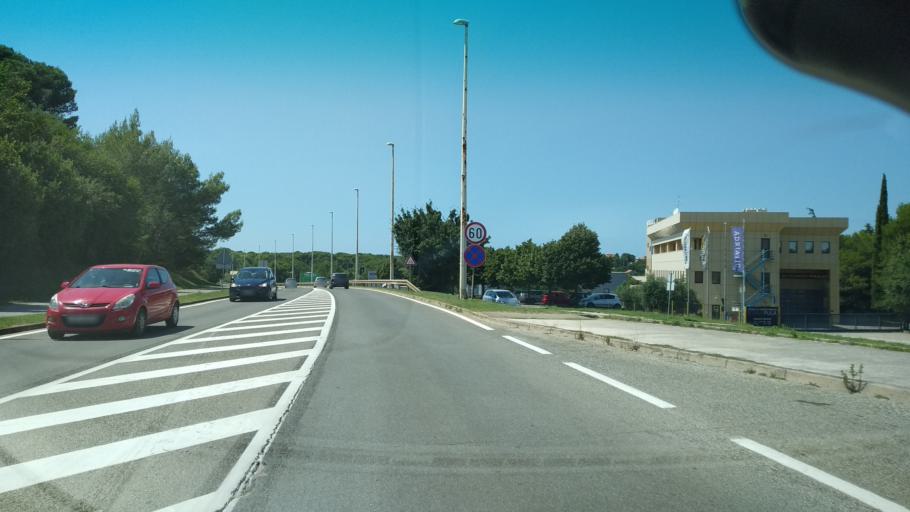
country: HR
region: Istarska
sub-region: Grad Pula
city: Pula
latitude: 44.8860
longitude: 13.8564
